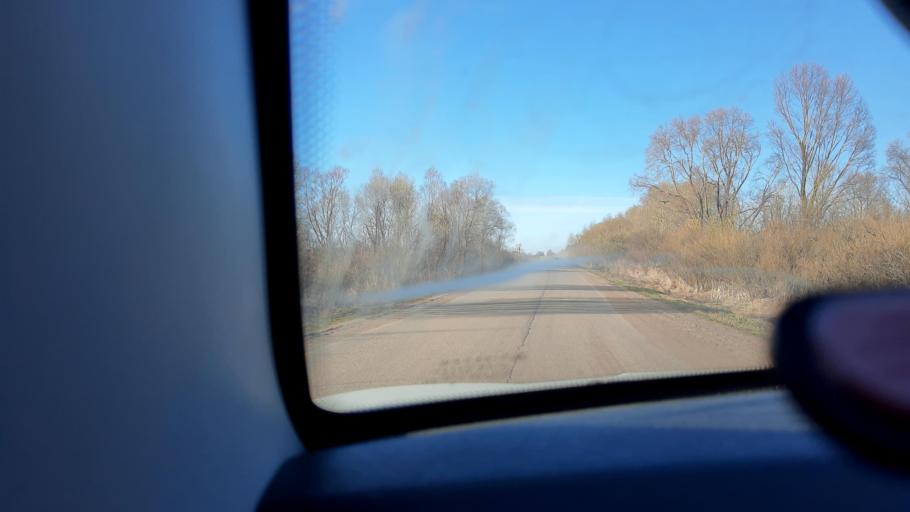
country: RU
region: Bashkortostan
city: Asanovo
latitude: 54.8496
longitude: 55.4556
